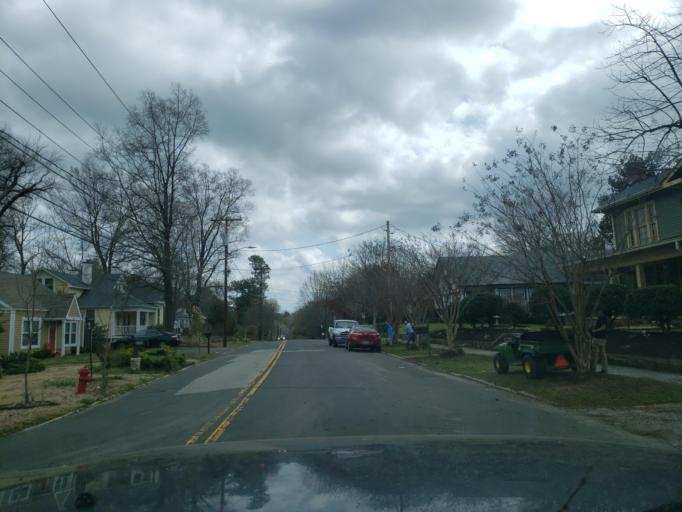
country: US
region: North Carolina
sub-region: Durham County
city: Durham
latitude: 35.9867
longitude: -78.9242
